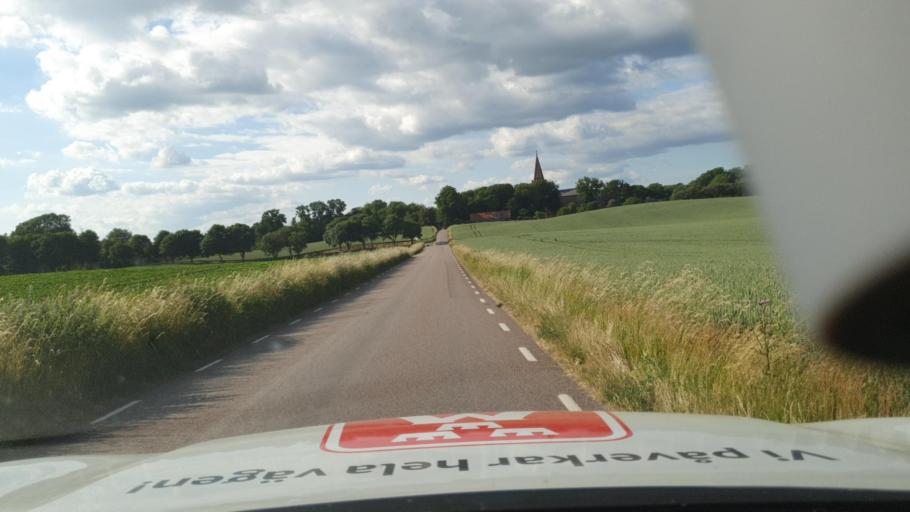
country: SE
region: Skane
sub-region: Ystads Kommun
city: Ystad
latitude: 55.4514
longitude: 13.7133
